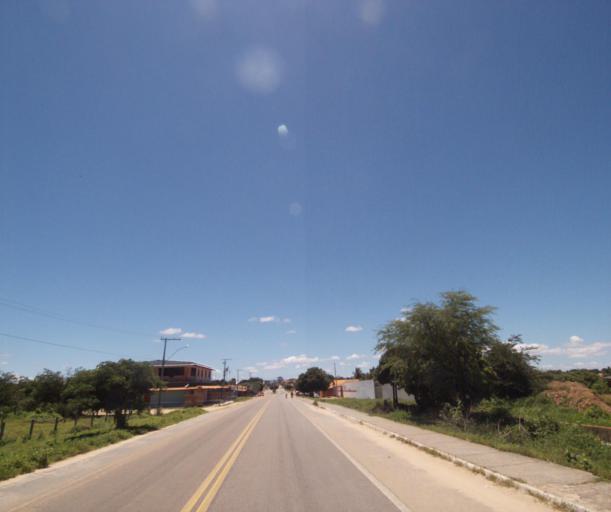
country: BR
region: Bahia
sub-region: Carinhanha
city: Carinhanha
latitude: -14.2930
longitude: -43.7766
